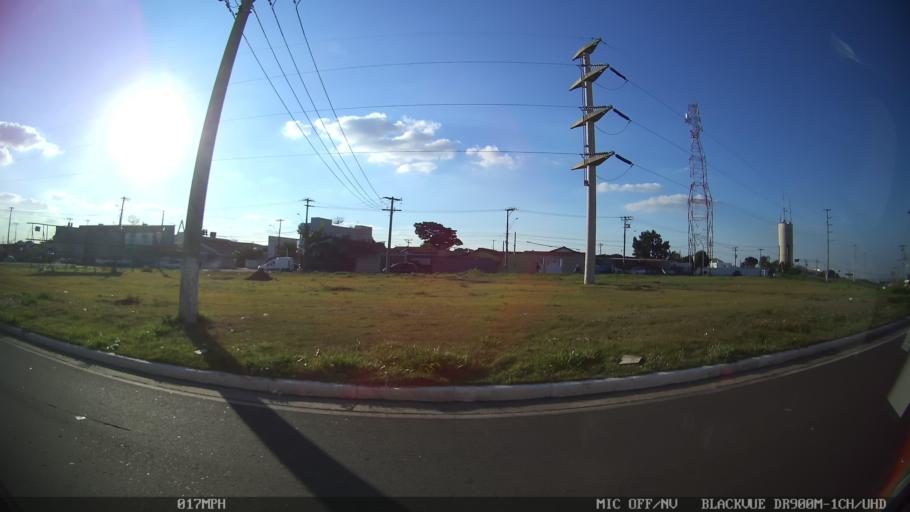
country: BR
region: Sao Paulo
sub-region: Americana
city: Americana
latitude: -22.7349
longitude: -47.3543
